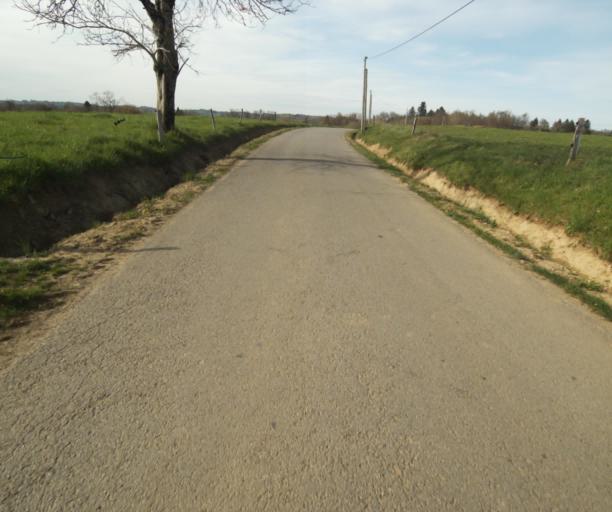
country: FR
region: Limousin
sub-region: Departement de la Correze
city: Naves
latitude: 45.3006
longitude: 1.7386
